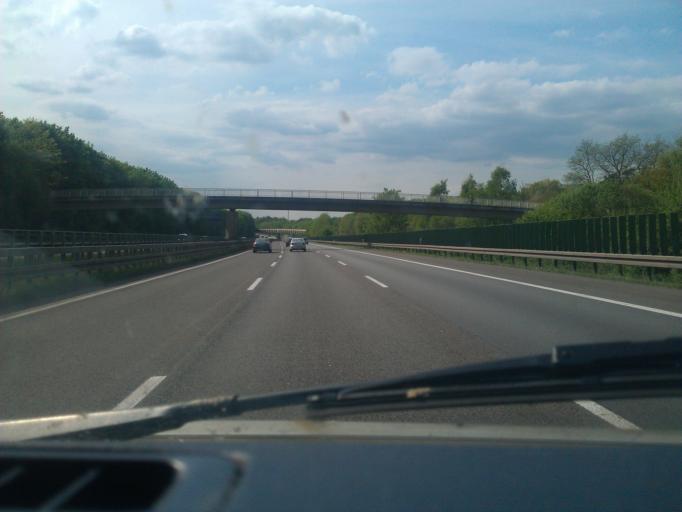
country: DE
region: North Rhine-Westphalia
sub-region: Regierungsbezirk Dusseldorf
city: Moers
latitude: 51.4868
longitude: 6.6607
